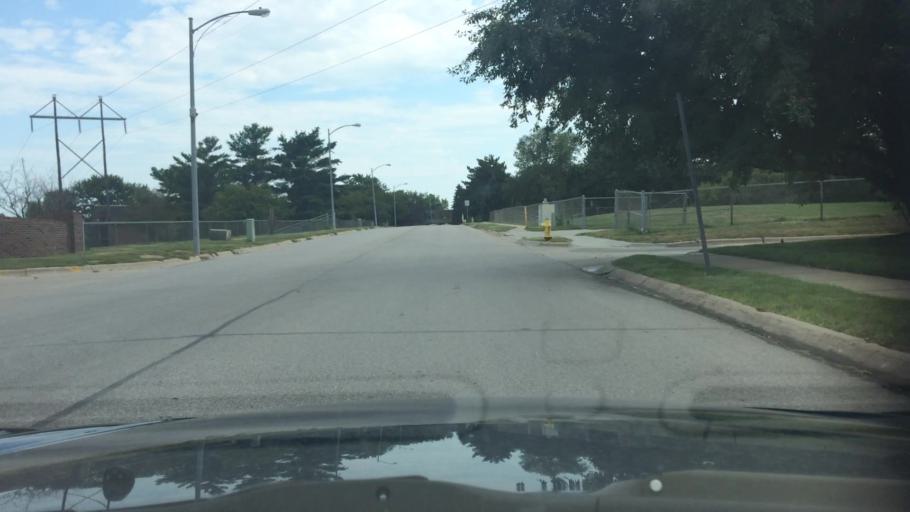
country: US
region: Nebraska
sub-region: Douglas County
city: Ralston
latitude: 41.1978
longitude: -96.0688
